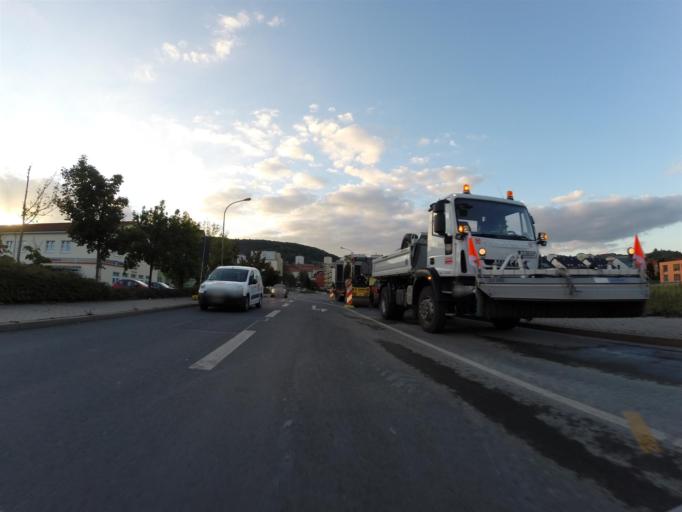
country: DE
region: Thuringia
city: Jena
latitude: 50.9473
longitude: 11.6053
